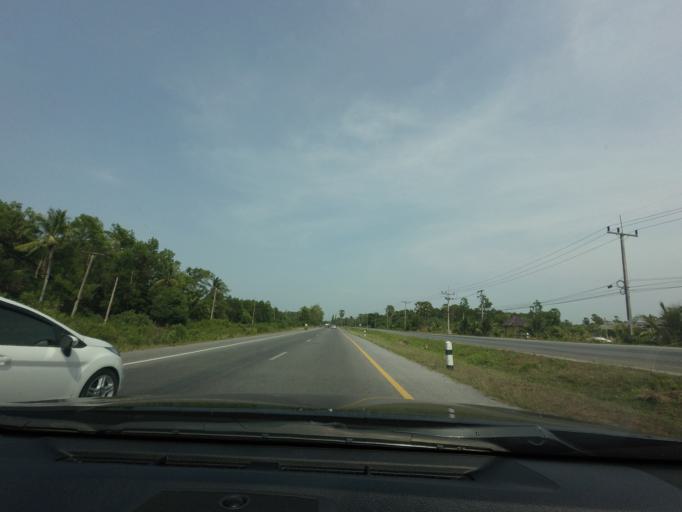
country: TH
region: Pattani
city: Yaring
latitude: 6.8253
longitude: 101.3956
